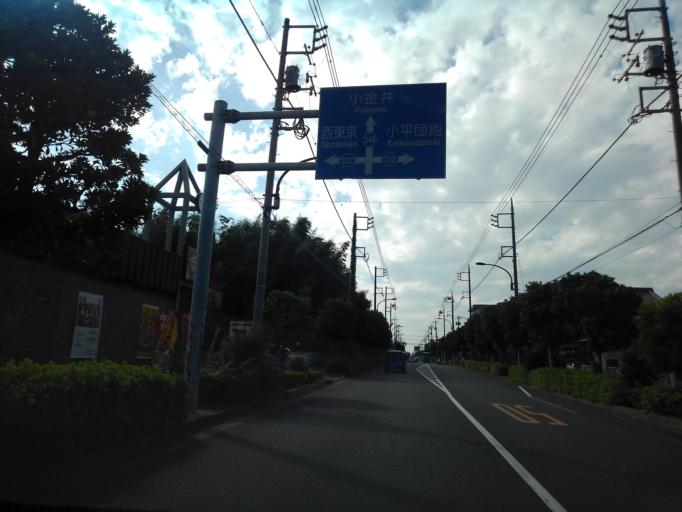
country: JP
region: Tokyo
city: Kokubunji
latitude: 35.7237
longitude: 139.4976
